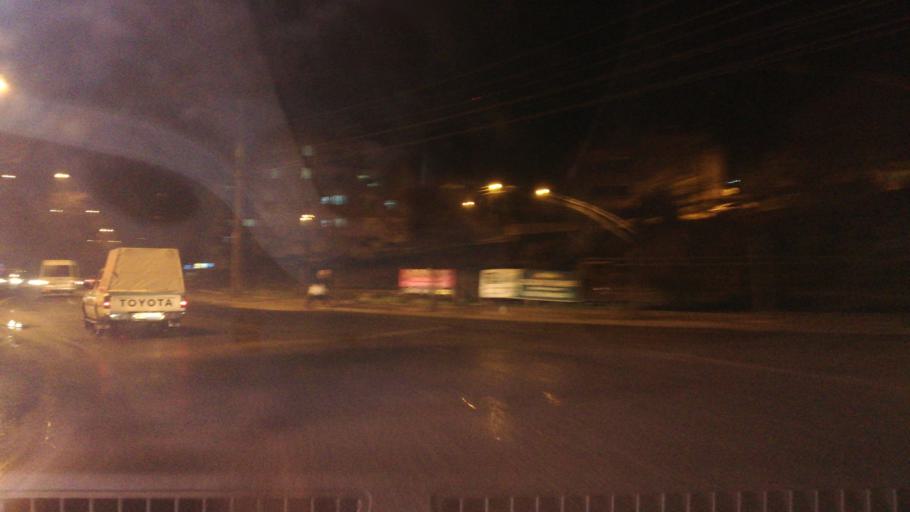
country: TR
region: Kahramanmaras
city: Kahramanmaras
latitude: 37.5867
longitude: 36.9452
